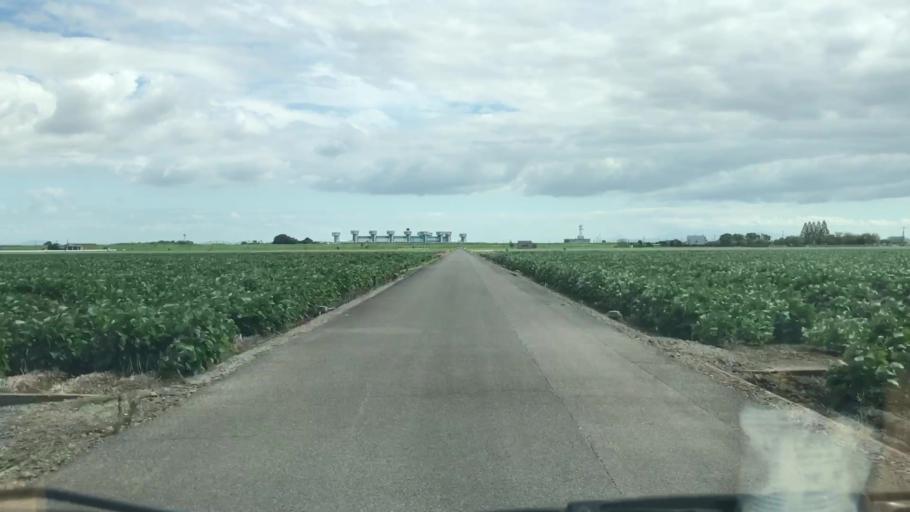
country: JP
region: Saga Prefecture
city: Saga-shi
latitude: 33.2130
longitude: 130.1835
